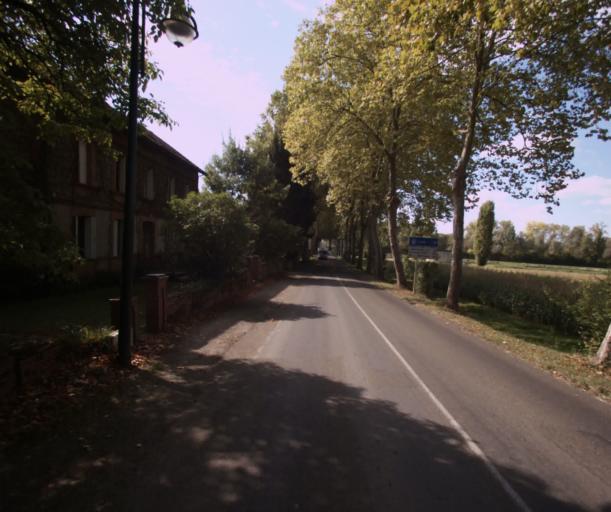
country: FR
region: Midi-Pyrenees
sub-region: Departement du Gers
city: Cazaubon
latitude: 43.9372
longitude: -0.0776
